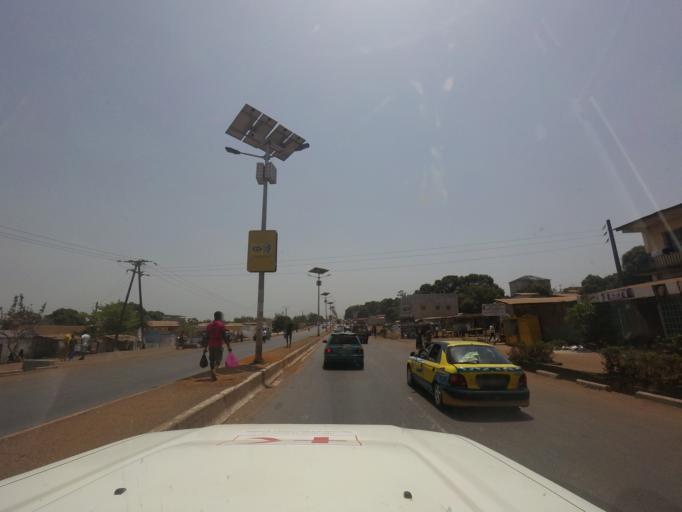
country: GN
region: Conakry
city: Conakry
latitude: 9.6307
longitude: -13.5746
